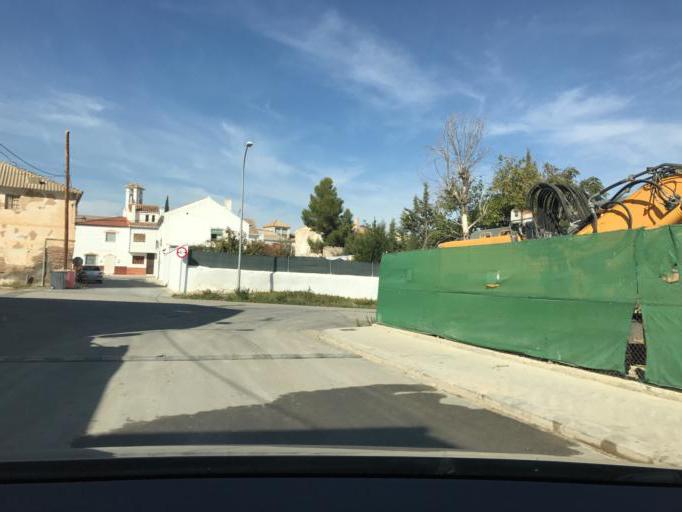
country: ES
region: Andalusia
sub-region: Provincia de Granada
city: Ventas de Huelma
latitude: 37.0839
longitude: -3.8057
